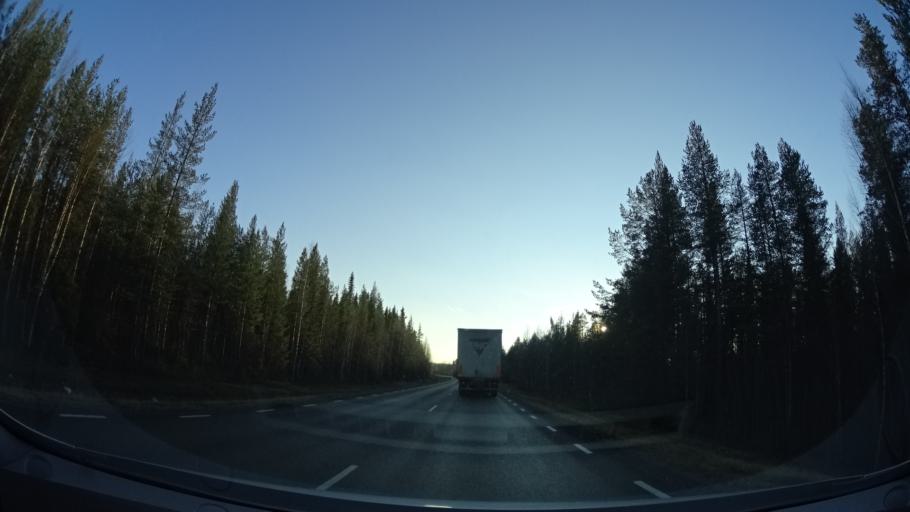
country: SE
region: Vaesterbotten
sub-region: Lycksele Kommun
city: Lycksele
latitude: 64.6589
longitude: 18.6634
